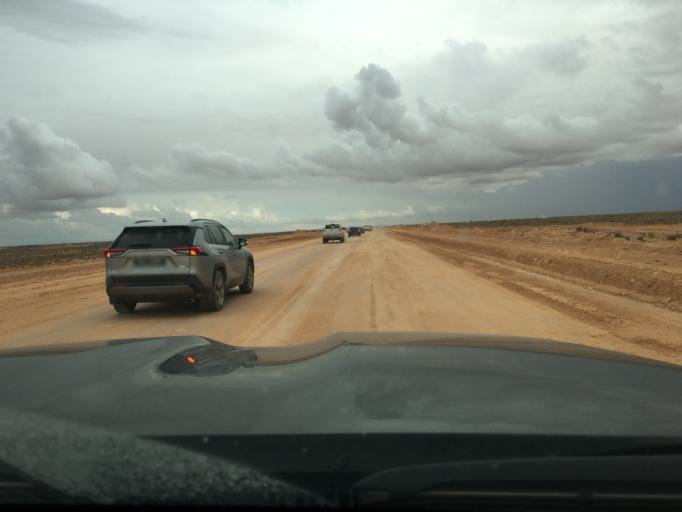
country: TN
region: Madanin
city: Medenine
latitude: 33.2746
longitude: 10.5901
